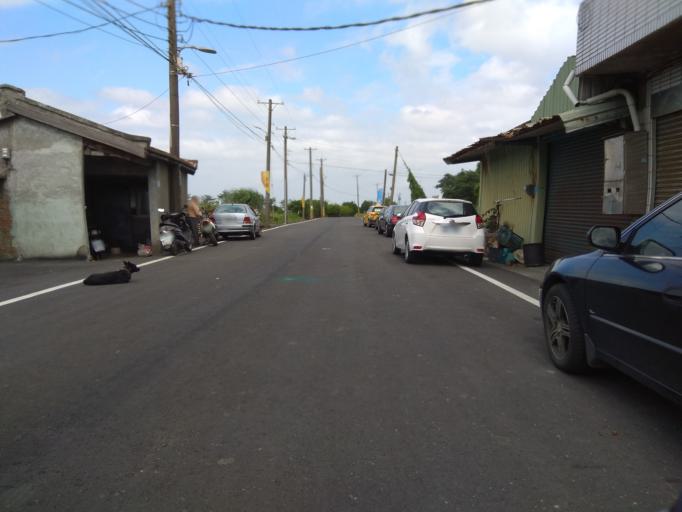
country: TW
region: Taiwan
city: Taoyuan City
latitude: 25.0618
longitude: 121.2310
